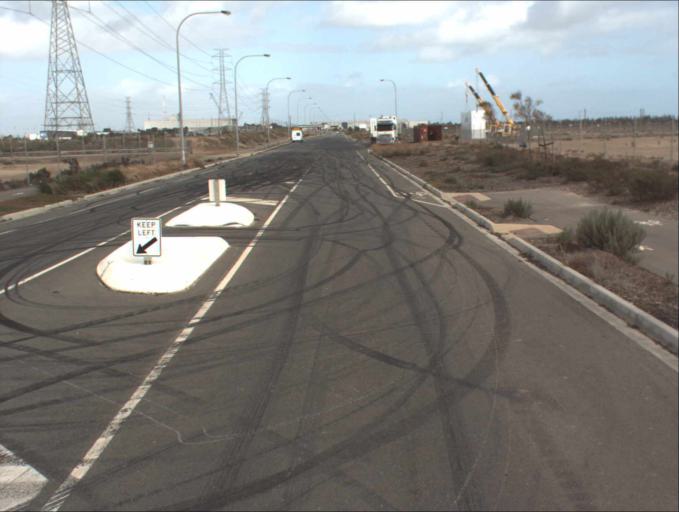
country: AU
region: South Australia
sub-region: Port Adelaide Enfield
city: Birkenhead
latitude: -34.7706
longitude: 138.5101
